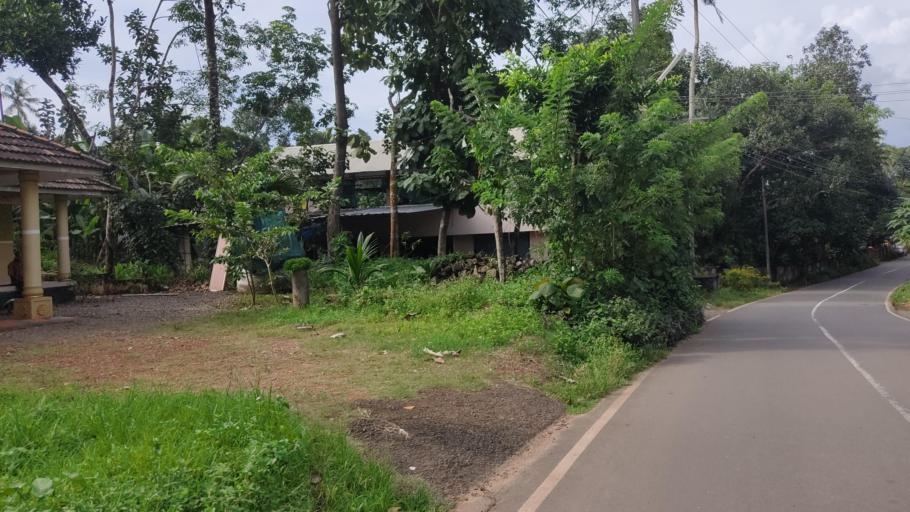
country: IN
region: Kerala
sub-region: Pattanamtitta
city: Adur
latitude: 9.1908
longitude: 76.7745
